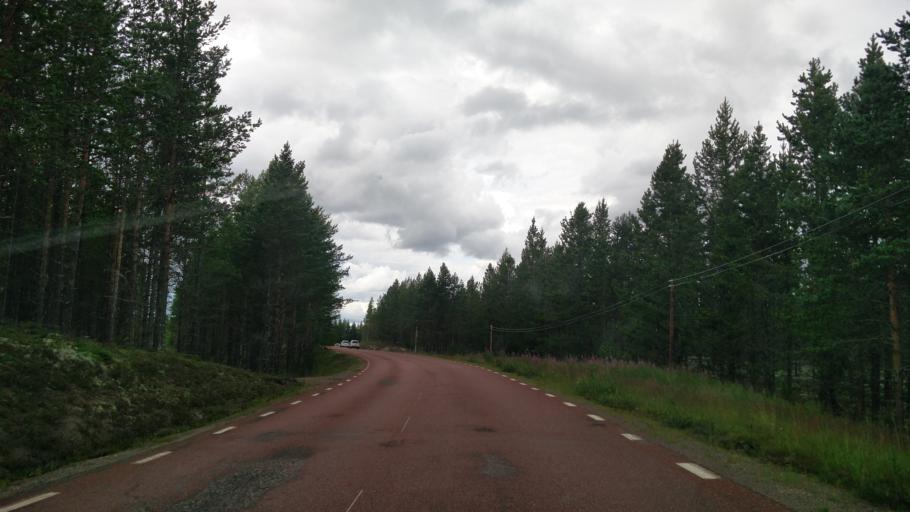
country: NO
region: Hedmark
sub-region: Trysil
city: Innbygda
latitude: 61.1448
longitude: 12.8064
